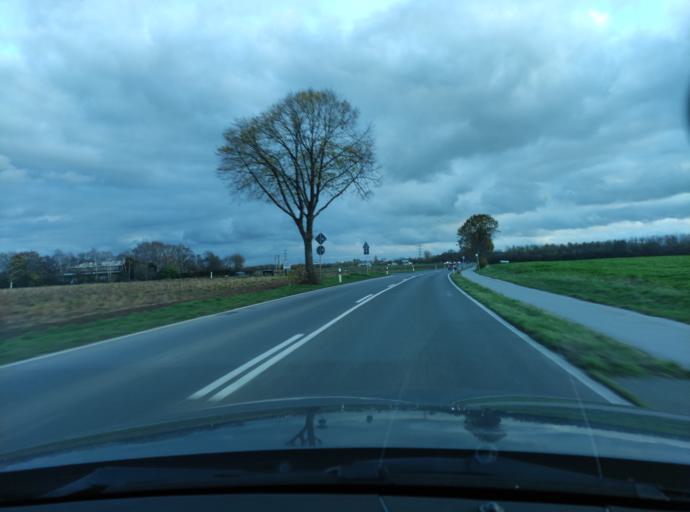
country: DE
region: North Rhine-Westphalia
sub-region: Regierungsbezirk Dusseldorf
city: Dormagen
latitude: 51.1101
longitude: 6.7809
